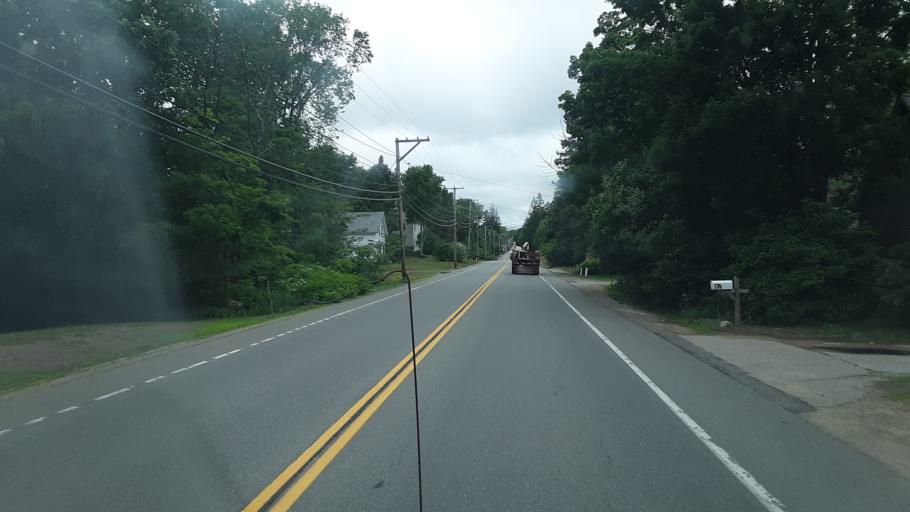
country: US
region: New Hampshire
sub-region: Rockingham County
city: Northwood
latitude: 43.1996
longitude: -71.1600
